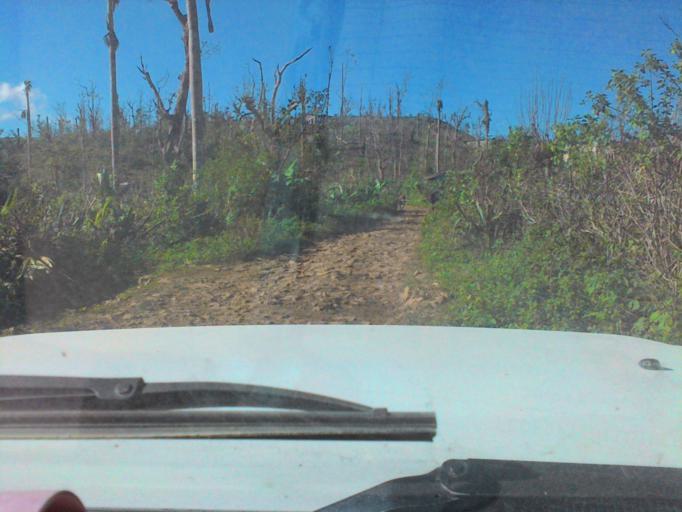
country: HT
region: Grandans
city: Jeremie
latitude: 18.4910
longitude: -74.1076
